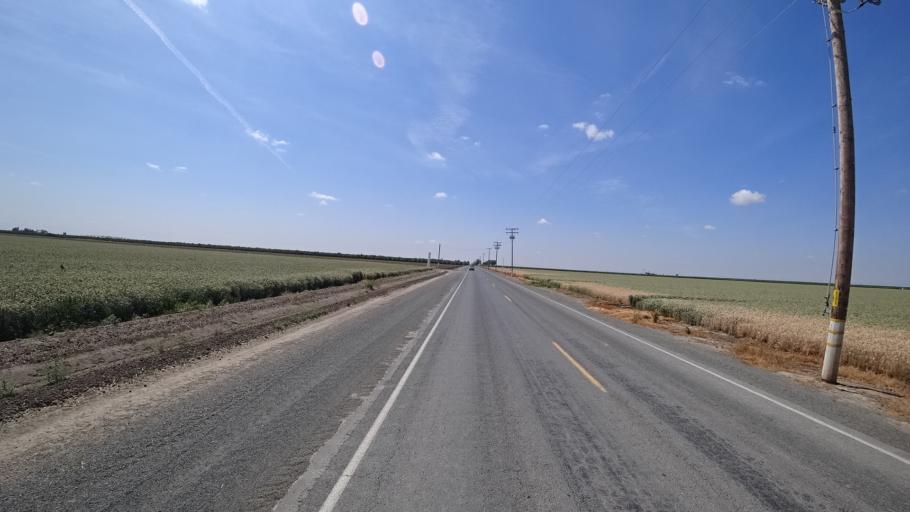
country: US
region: California
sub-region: Tulare County
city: Goshen
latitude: 36.2807
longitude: -119.4922
